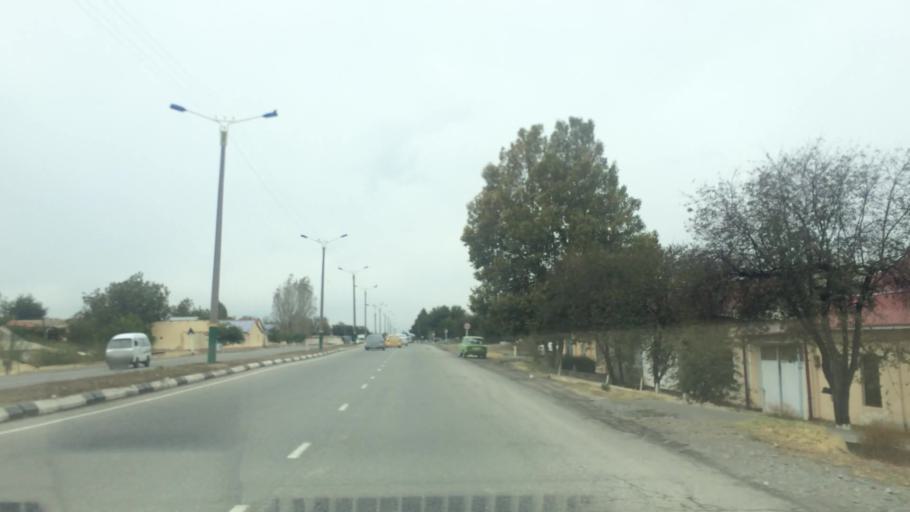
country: UZ
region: Samarqand
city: Bulung'ur
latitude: 39.7665
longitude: 67.2600
